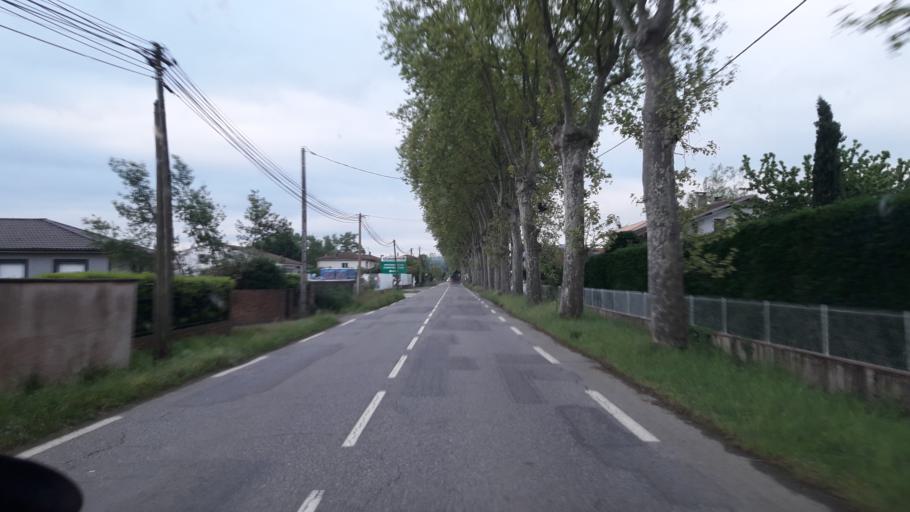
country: FR
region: Midi-Pyrenees
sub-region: Departement de la Haute-Garonne
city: Cazeres
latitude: 43.2224
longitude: 1.0849
